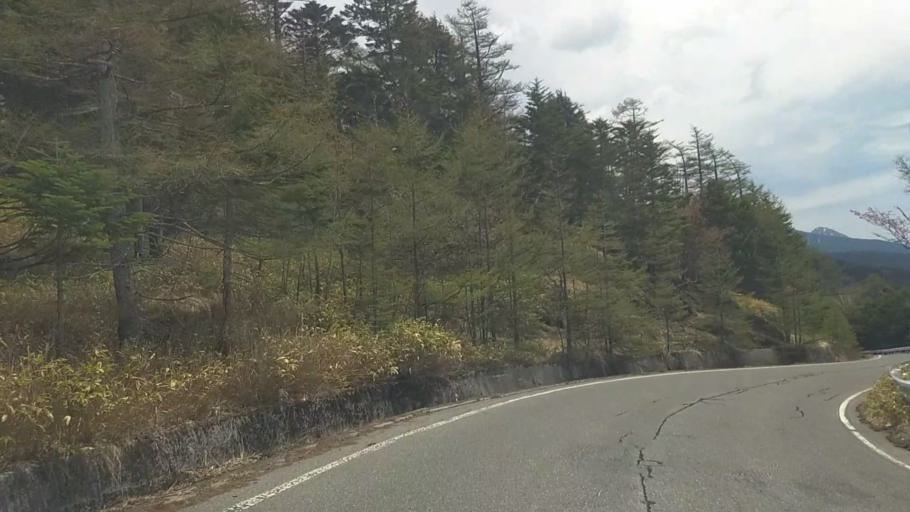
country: JP
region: Nagano
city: Chino
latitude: 36.0558
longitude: 138.3186
